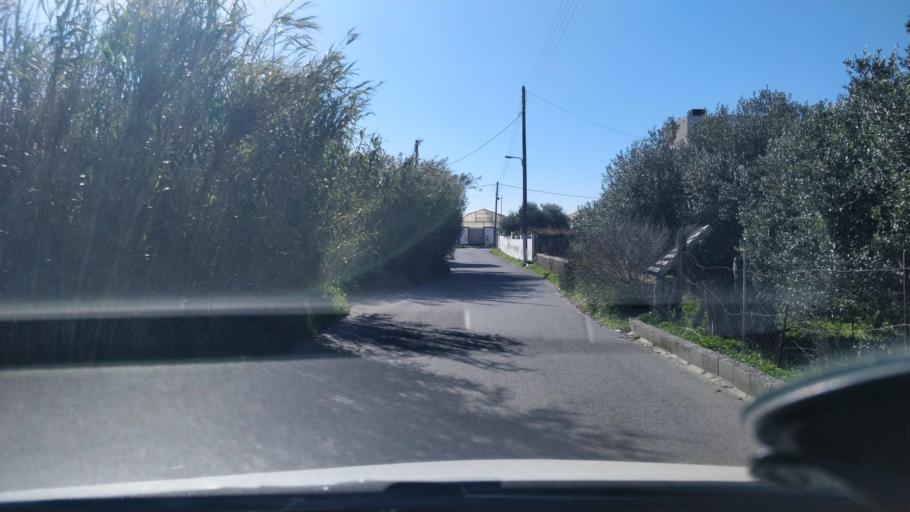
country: GR
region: Crete
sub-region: Nomos Lasithiou
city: Gra Liyia
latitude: 35.0143
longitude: 25.6770
